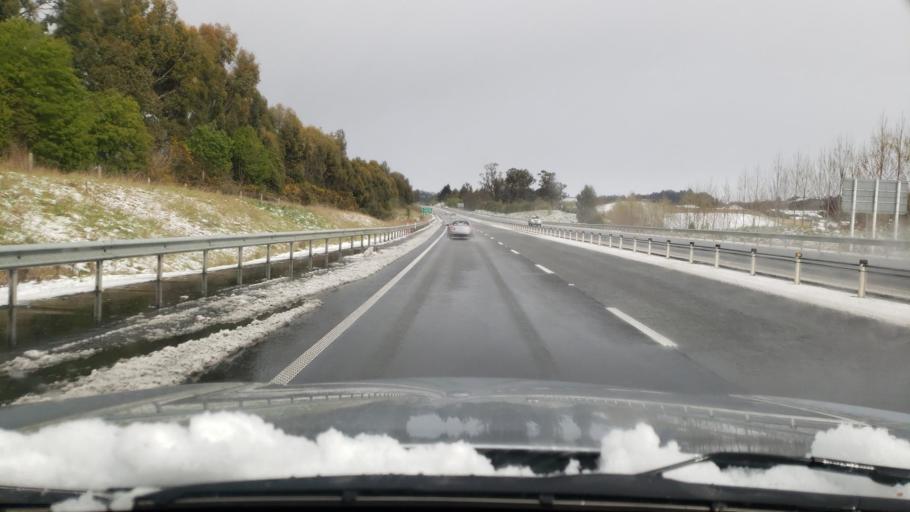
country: NZ
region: Otago
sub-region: Dunedin City
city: Dunedin
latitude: -45.9029
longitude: 170.4115
